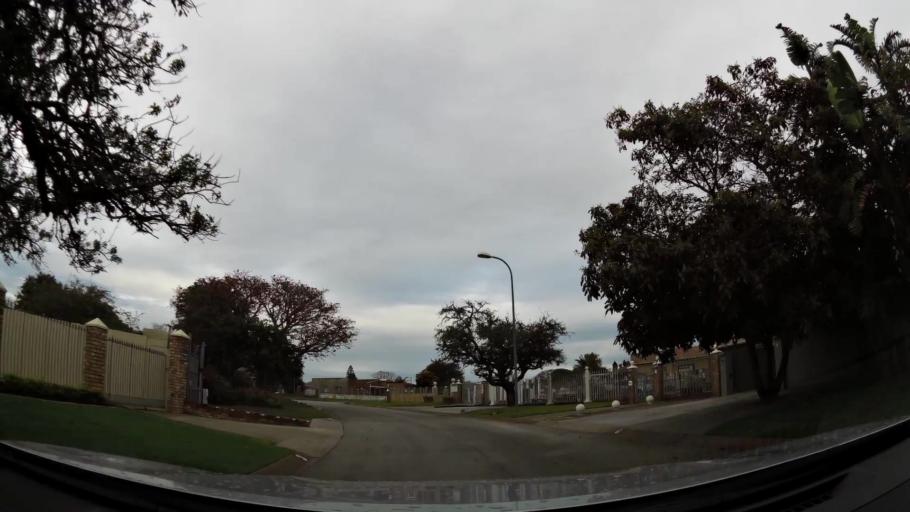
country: ZA
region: Eastern Cape
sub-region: Nelson Mandela Bay Metropolitan Municipality
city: Port Elizabeth
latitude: -33.9850
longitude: 25.5607
